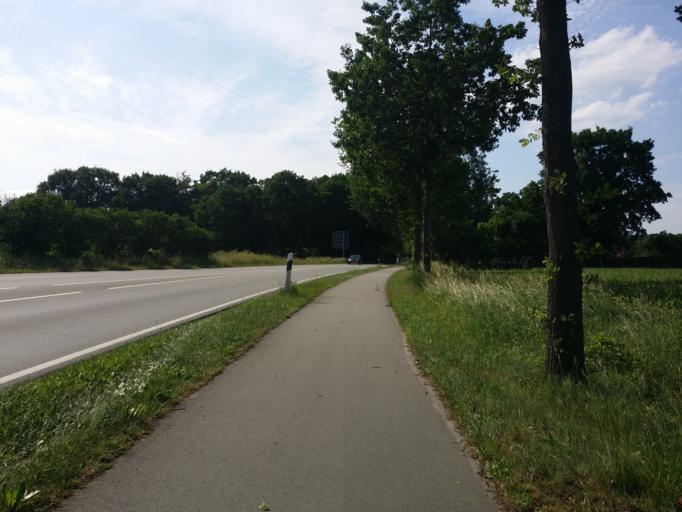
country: DE
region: Lower Saxony
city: Wiefelstede
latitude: 53.2413
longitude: 8.1572
